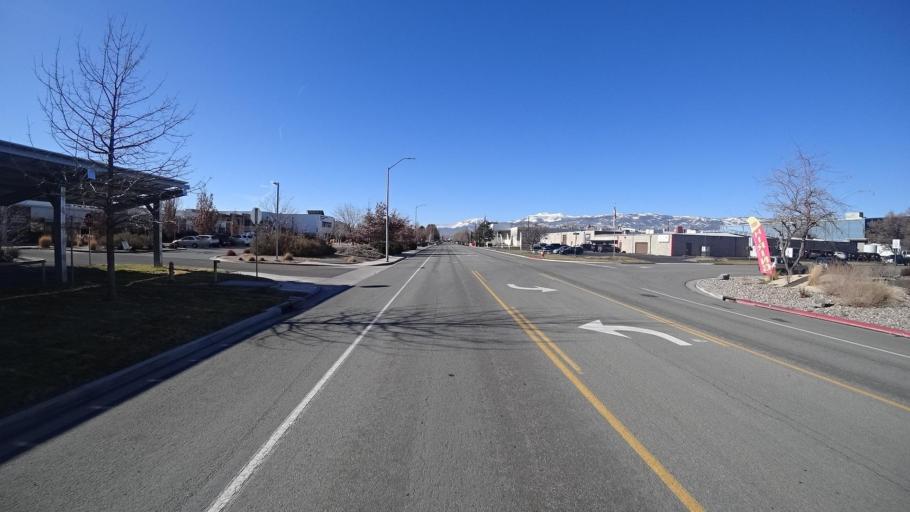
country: US
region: Nevada
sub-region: Washoe County
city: Sparks
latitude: 39.5073
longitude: -119.7553
